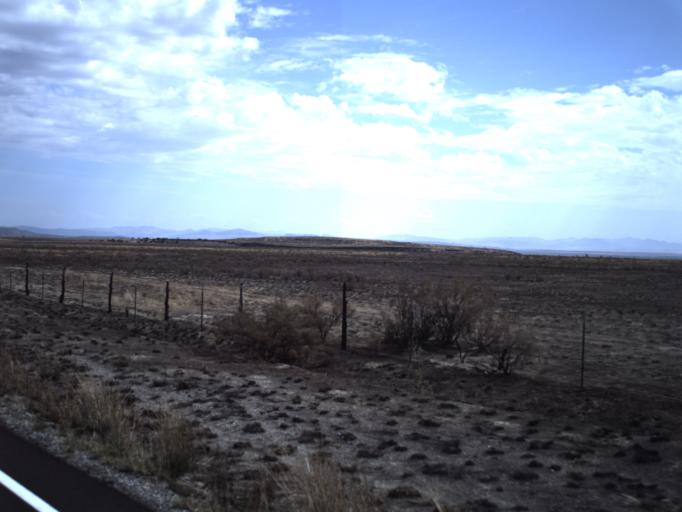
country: US
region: Idaho
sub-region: Minidoka County
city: Rupert
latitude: 41.8248
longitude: -113.1797
